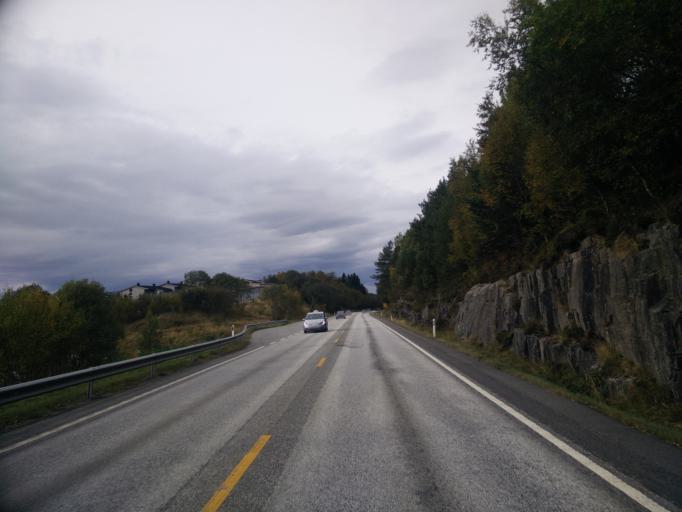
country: NO
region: More og Romsdal
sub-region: Haram
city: Brattvag
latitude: 62.4713
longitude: 6.3786
